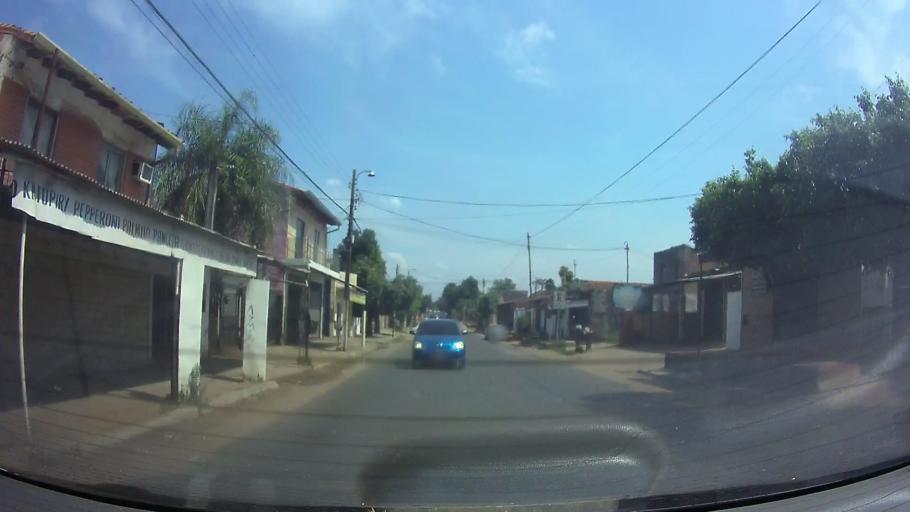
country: PY
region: Central
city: San Lorenzo
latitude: -25.3455
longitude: -57.4928
